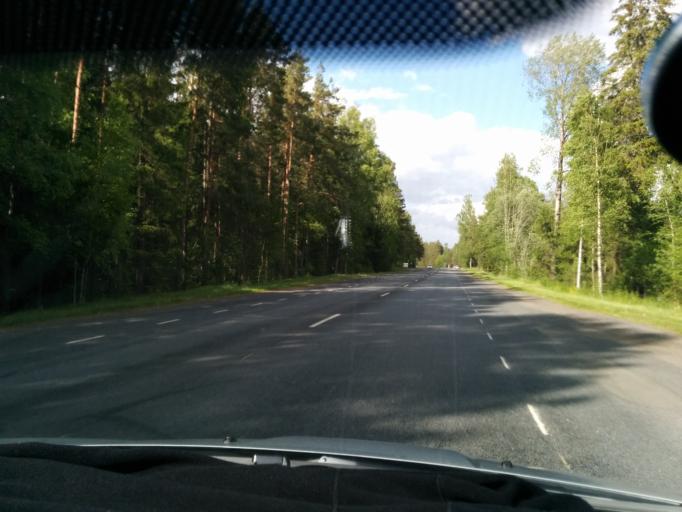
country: EE
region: Harju
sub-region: Loksa linn
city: Loksa
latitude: 59.5384
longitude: 25.7327
